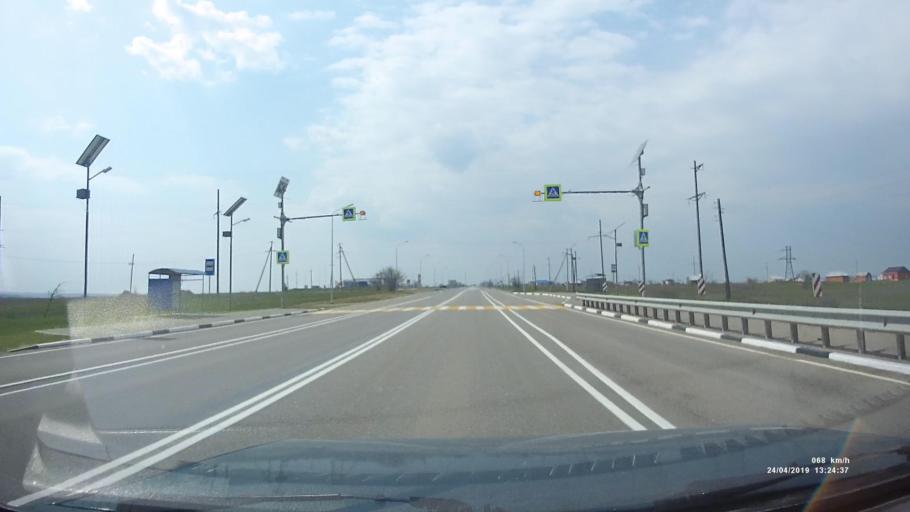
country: RU
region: Kalmykiya
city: Elista
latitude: 46.2846
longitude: 44.2527
